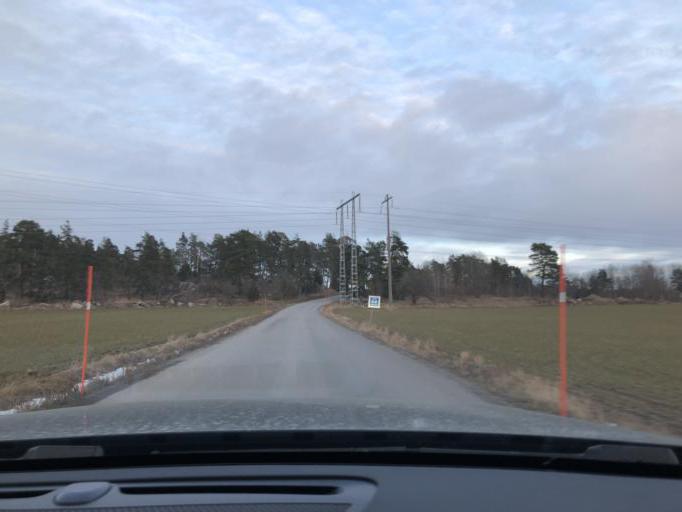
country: SE
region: Uppsala
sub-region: Uppsala Kommun
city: Gamla Uppsala
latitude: 59.9203
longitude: 17.6429
